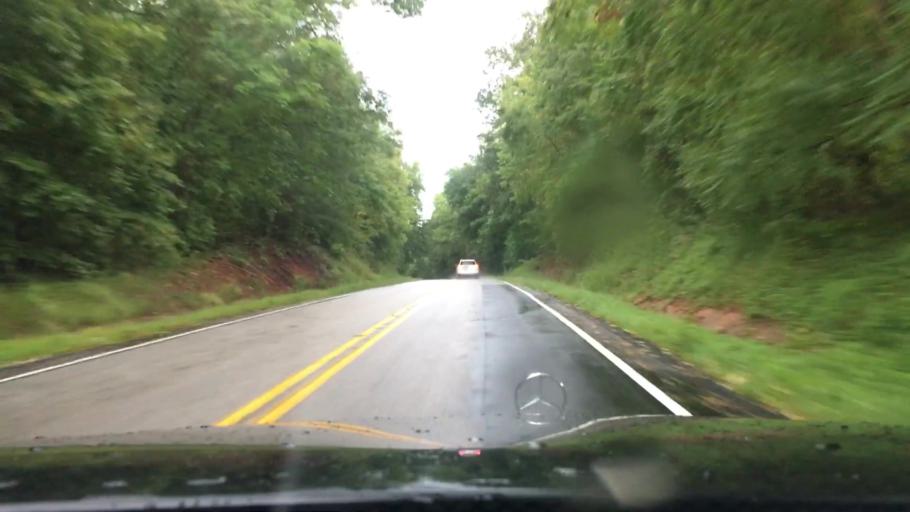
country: US
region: Virginia
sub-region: Amherst County
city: Amherst
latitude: 37.6873
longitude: -79.0252
